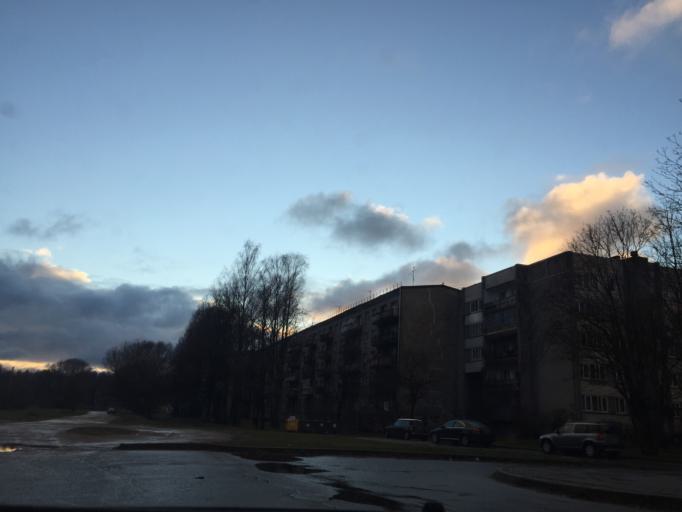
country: LV
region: Riga
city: Riga
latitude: 56.9409
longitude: 24.0818
